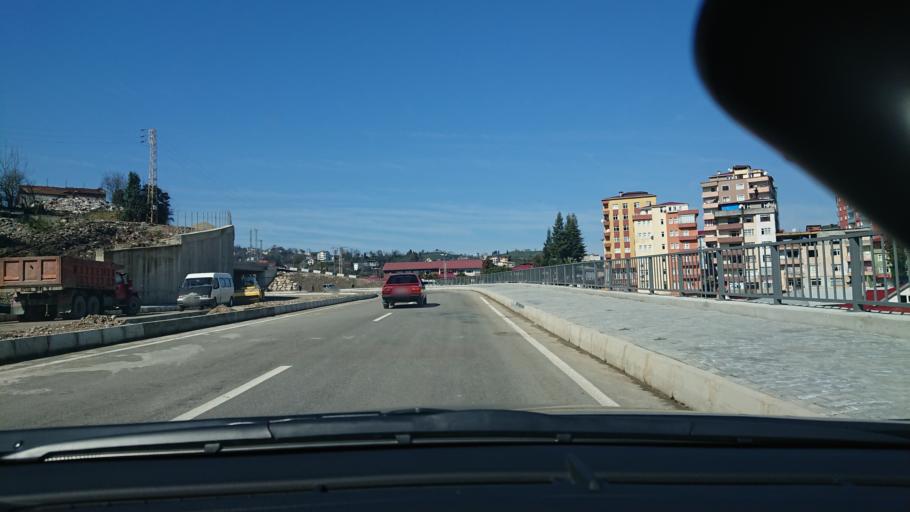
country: TR
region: Rize
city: Rize
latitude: 41.0152
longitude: 40.5131
